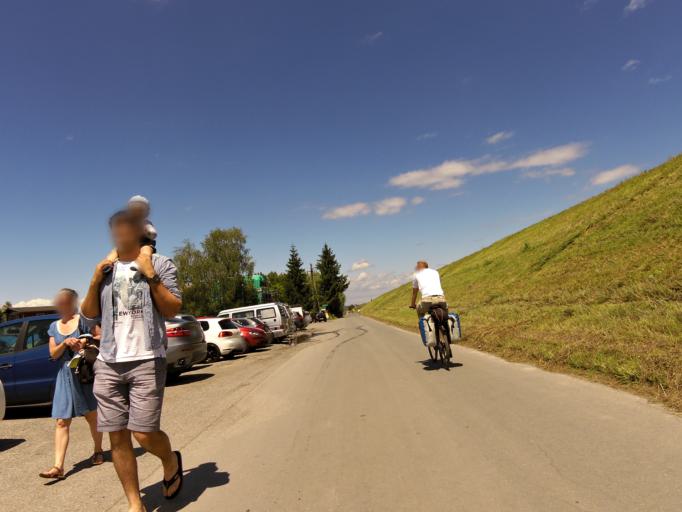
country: AT
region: Vorarlberg
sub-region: Politischer Bezirk Bregenz
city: Fussach
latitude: 47.4869
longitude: 9.6680
